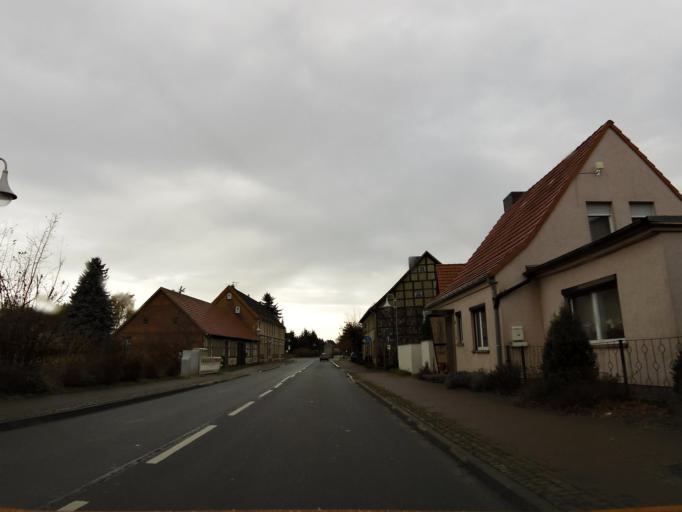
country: DE
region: Saxony-Anhalt
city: Gardelegen
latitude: 52.5756
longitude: 11.3586
